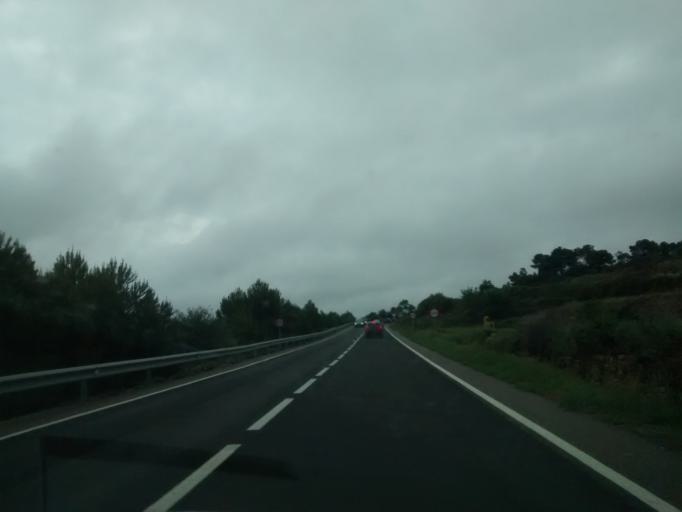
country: ES
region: Catalonia
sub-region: Provincia de Tarragona
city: Bot
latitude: 41.0523
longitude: 0.3640
